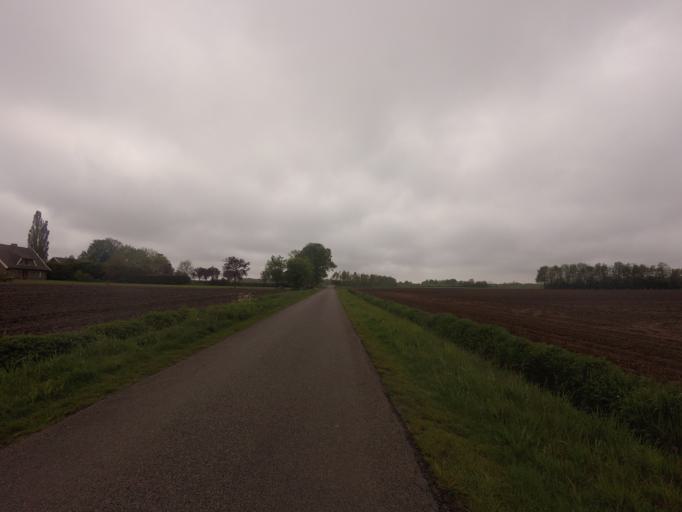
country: NL
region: Overijssel
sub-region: Gemeente Haaksbergen
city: Haaksbergen
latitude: 52.1375
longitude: 6.7980
